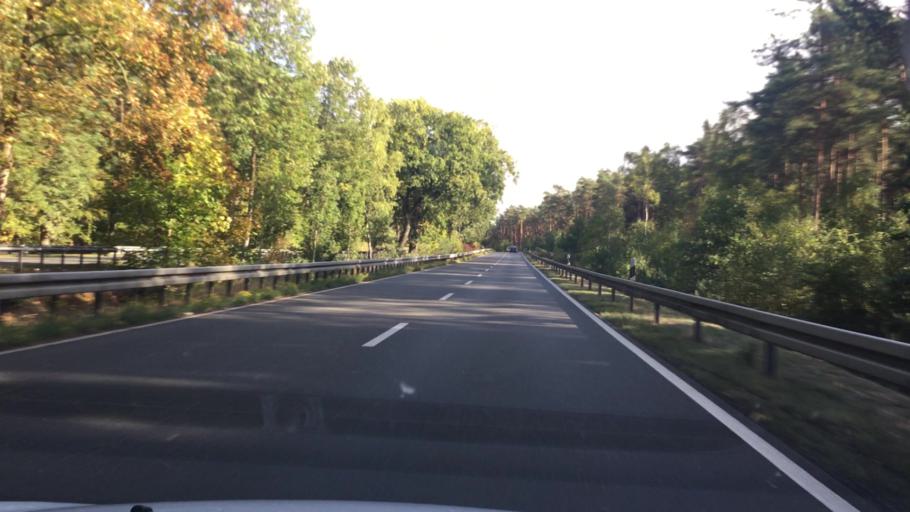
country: DE
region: Lower Saxony
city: Linsburg
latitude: 52.5437
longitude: 9.3704
